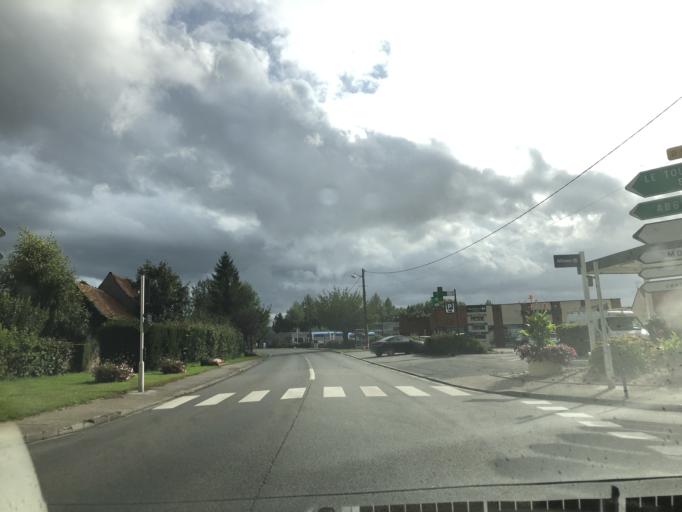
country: FR
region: Nord-Pas-de-Calais
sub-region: Departement du Pas-de-Calais
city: Wailly
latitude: 50.5996
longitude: 2.0962
